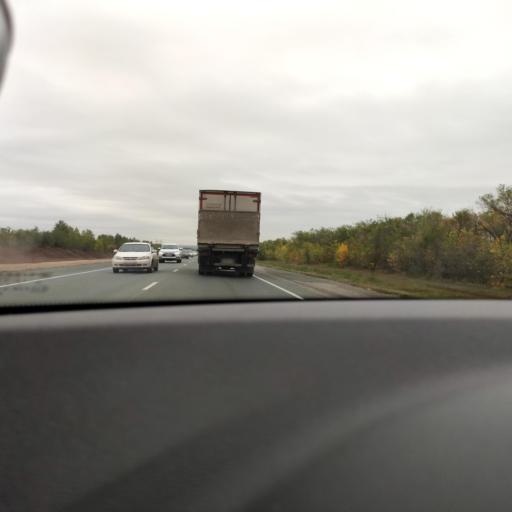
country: RU
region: Samara
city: Krasnyy Yar
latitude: 53.4636
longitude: 50.3952
